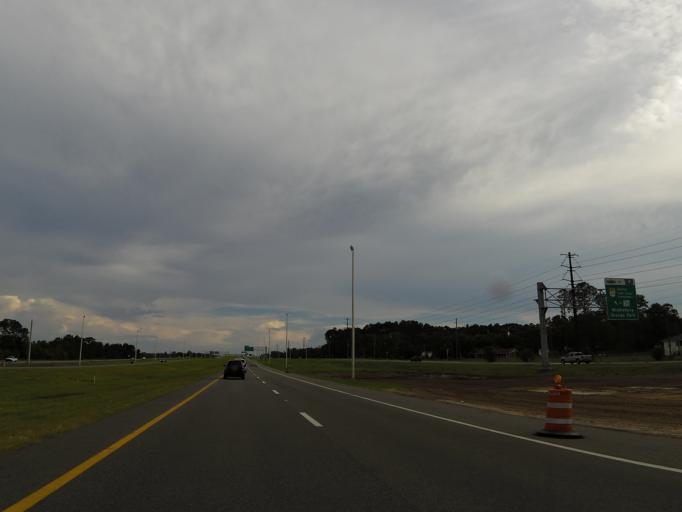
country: US
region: Florida
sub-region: Clay County
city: Lakeside
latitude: 30.1435
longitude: -81.8310
